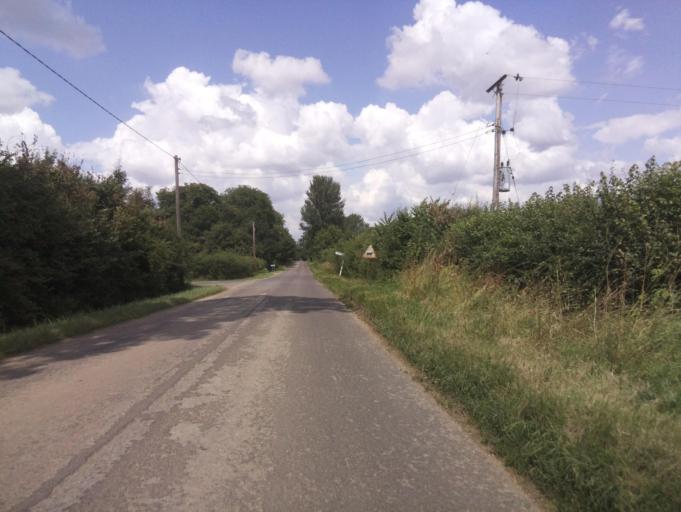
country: GB
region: England
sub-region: Wiltshire
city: Minety
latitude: 51.6078
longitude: -1.9534
